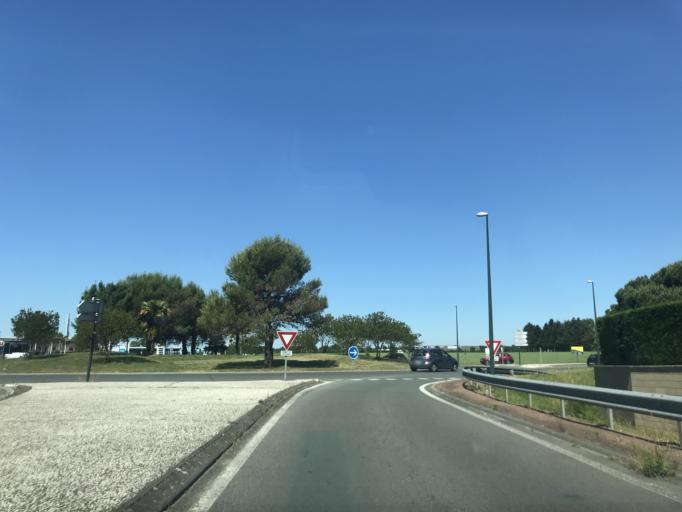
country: FR
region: Poitou-Charentes
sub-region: Departement de la Charente-Maritime
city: Gemozac
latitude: 45.5766
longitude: -0.6751
